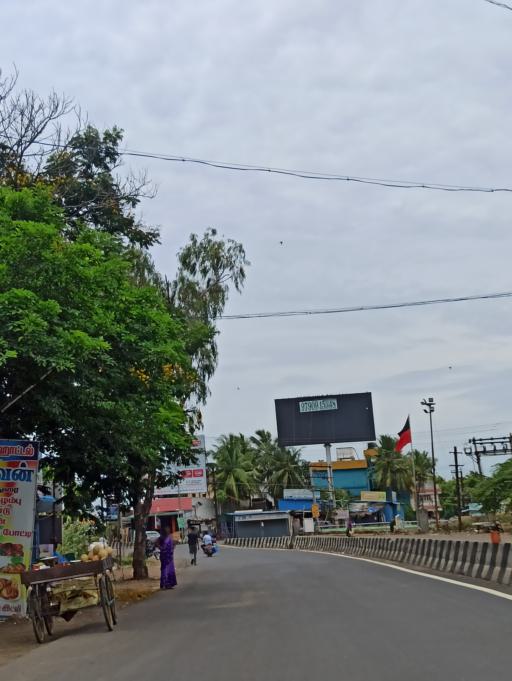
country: IN
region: Tamil Nadu
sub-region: Kancheepuram
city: Vandalur
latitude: 12.9157
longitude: 80.0779
